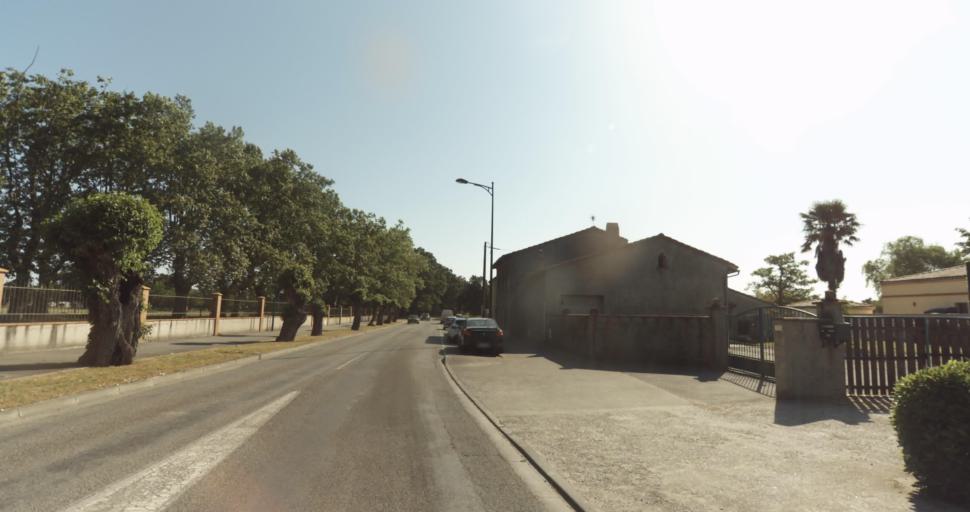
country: FR
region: Midi-Pyrenees
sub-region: Departement de la Haute-Garonne
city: Tournefeuille
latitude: 43.5655
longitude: 1.3220
